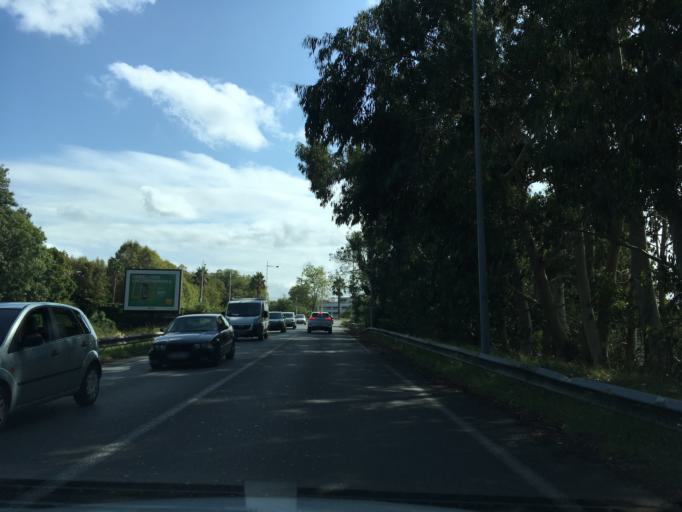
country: FR
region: Aquitaine
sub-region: Departement des Pyrenees-Atlantiques
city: Bayonne
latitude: 43.4873
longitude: -1.4903
